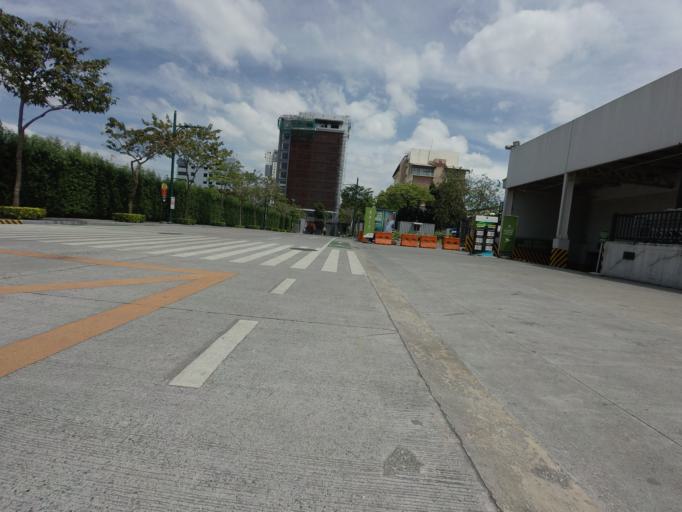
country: PH
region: Metro Manila
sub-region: Pasig
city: Pasig City
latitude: 14.5790
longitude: 121.0771
